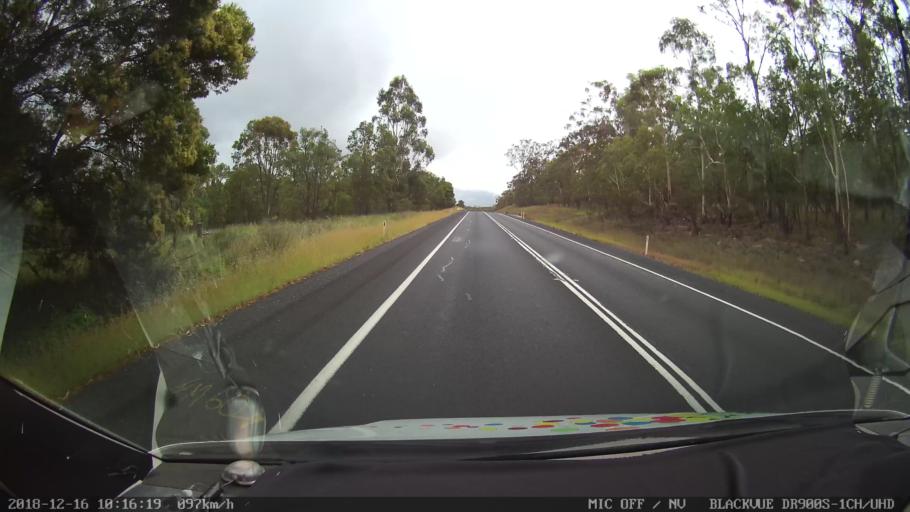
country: AU
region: New South Wales
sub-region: Tenterfield Municipality
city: Carrolls Creek
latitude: -29.2680
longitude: 151.9816
